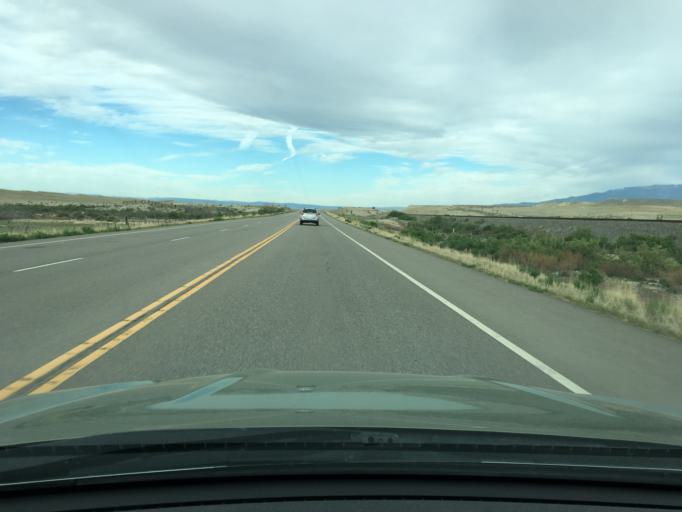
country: US
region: Colorado
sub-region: Delta County
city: Orchard City
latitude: 38.8024
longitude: -107.8897
